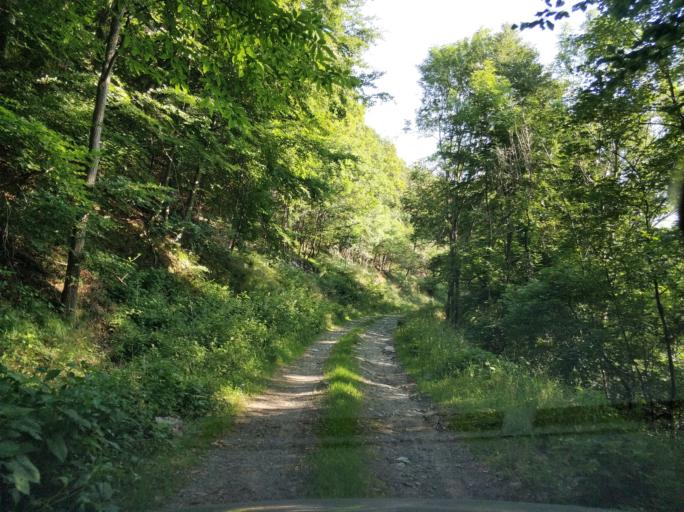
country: IT
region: Piedmont
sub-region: Provincia di Torino
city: Ceres
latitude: 45.3097
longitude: 7.3622
